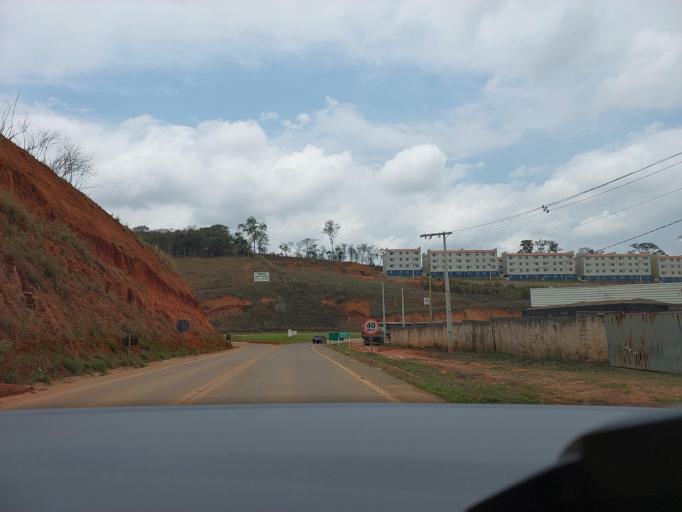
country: BR
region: Minas Gerais
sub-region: Ponte Nova
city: Ponte Nova
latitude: -20.3947
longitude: -42.8715
